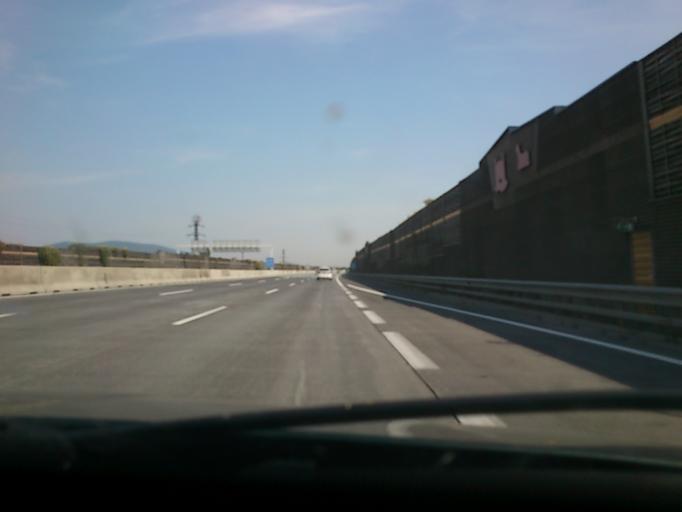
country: AT
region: Lower Austria
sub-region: Politischer Bezirk Baden
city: Kottingbrunn
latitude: 47.9547
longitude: 16.2207
